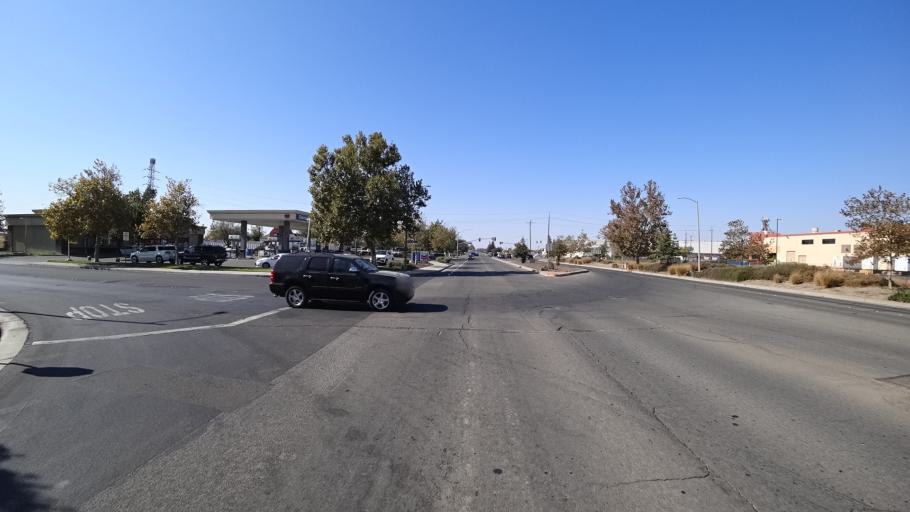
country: US
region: California
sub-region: Yolo County
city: Woodland
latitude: 38.6770
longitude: -121.7268
